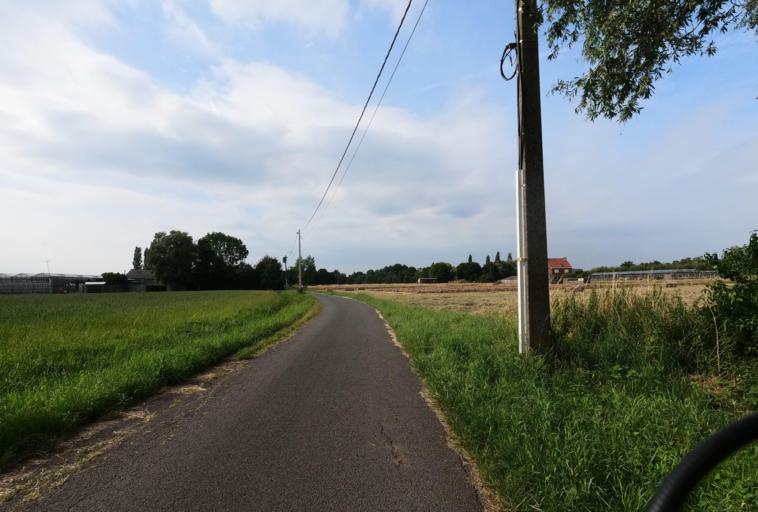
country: BE
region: Flanders
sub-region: Provincie Antwerpen
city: Putte
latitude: 51.0487
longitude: 4.6025
